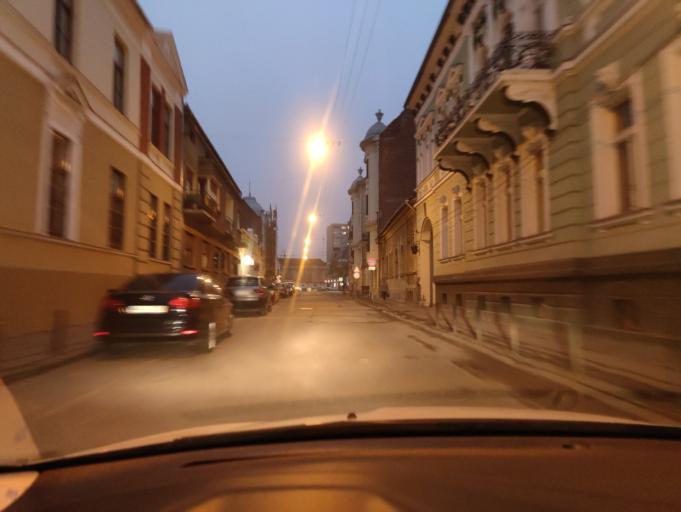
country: RO
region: Bihor
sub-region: Comuna Biharea
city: Oradea
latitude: 47.0587
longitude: 21.9302
